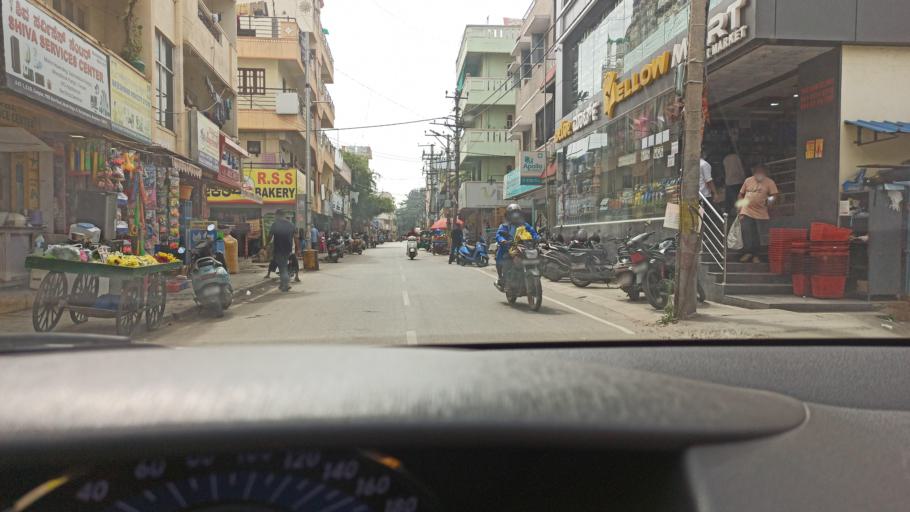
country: IN
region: Karnataka
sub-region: Bangalore Urban
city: Bangalore
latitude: 12.9923
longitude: 77.6804
